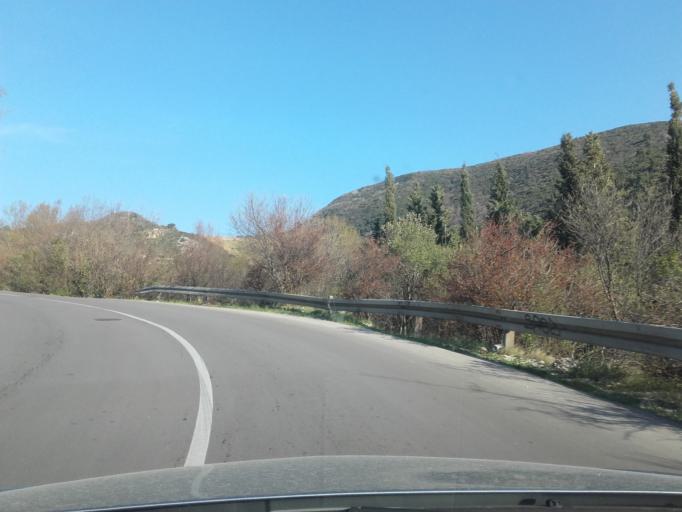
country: ME
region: Budva
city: Budva
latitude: 42.2899
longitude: 18.8282
